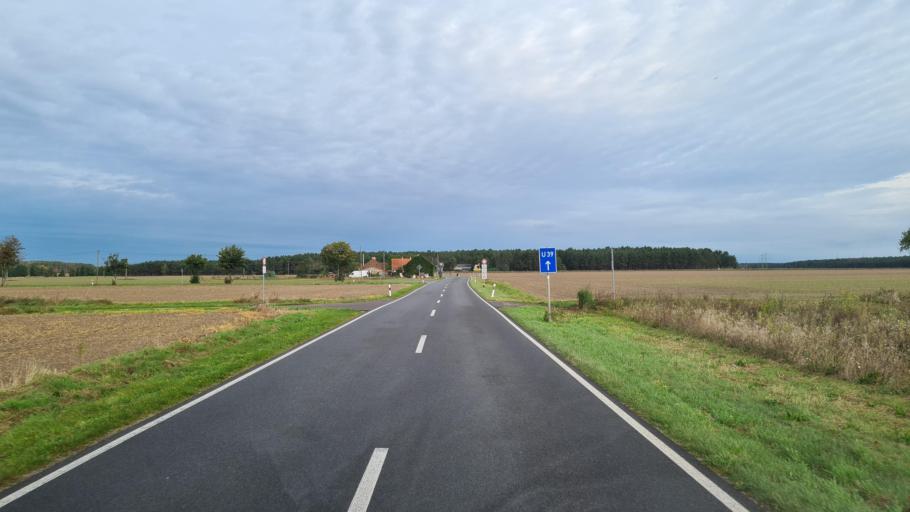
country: DE
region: Brandenburg
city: Luckau
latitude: 51.8817
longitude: 13.7193
